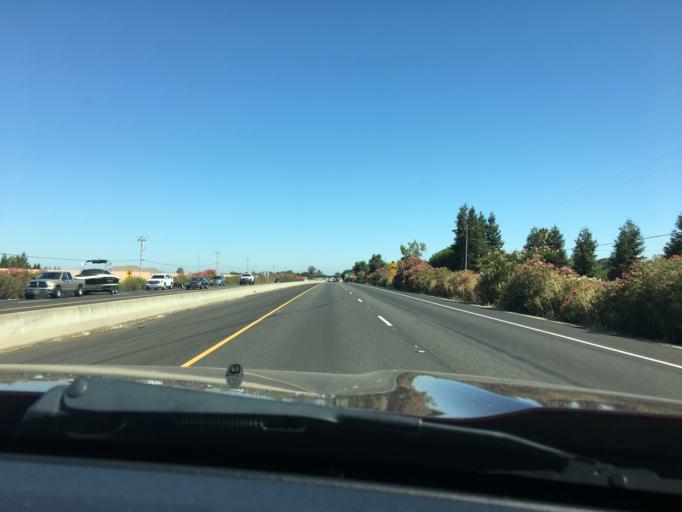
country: US
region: California
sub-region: San Joaquin County
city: Collierville
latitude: 38.2257
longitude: -121.2753
